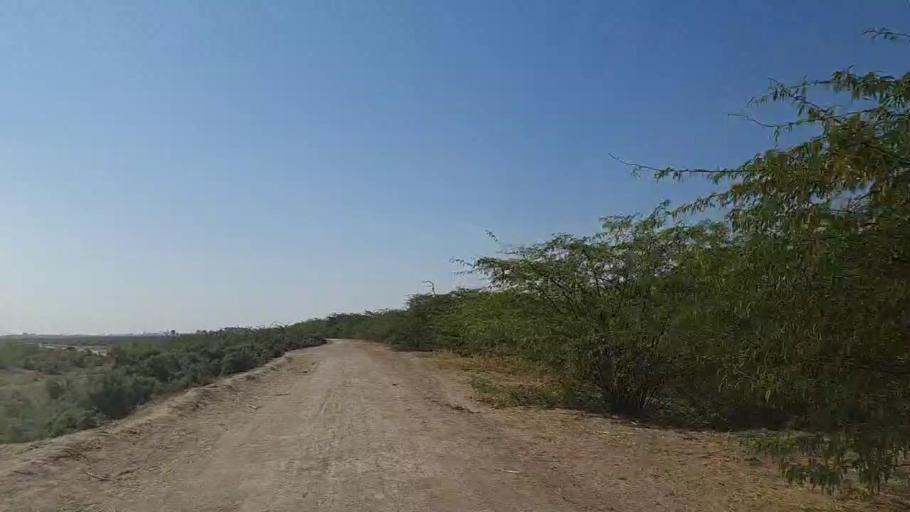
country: PK
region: Sindh
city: Pithoro
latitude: 25.4222
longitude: 69.3761
